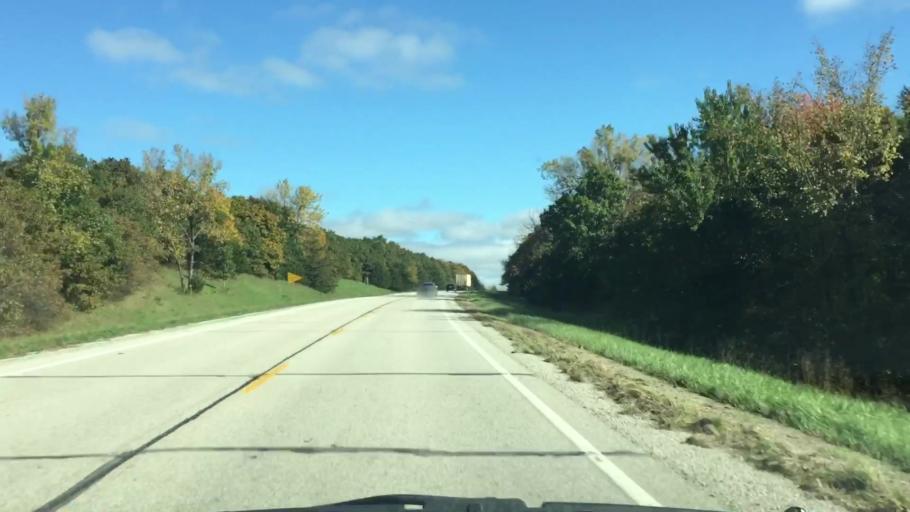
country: US
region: Iowa
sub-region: Decatur County
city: Leon
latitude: 40.6682
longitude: -93.7915
